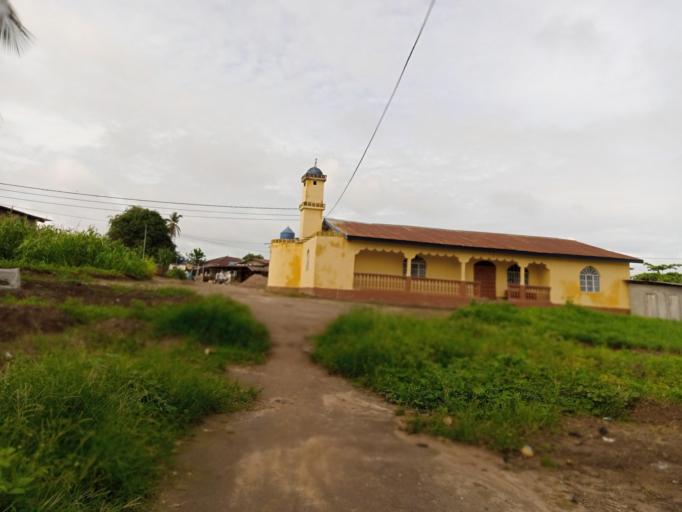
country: SL
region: Northern Province
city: Masoyila
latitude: 8.6027
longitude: -13.2007
